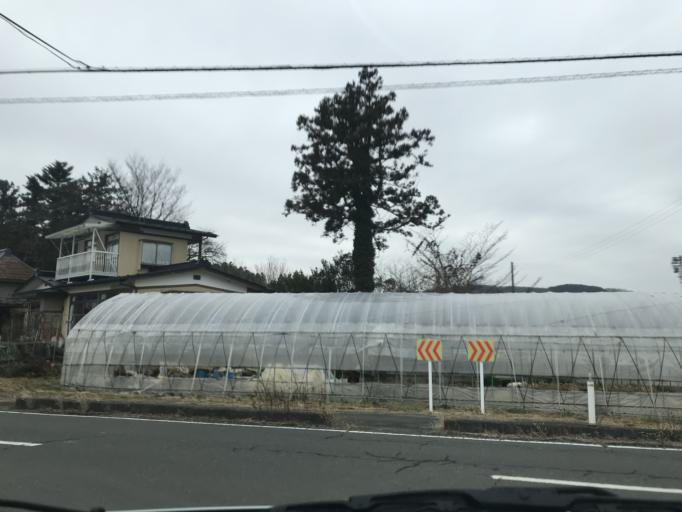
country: JP
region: Iwate
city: Ichinoseki
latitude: 38.7360
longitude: 141.2208
